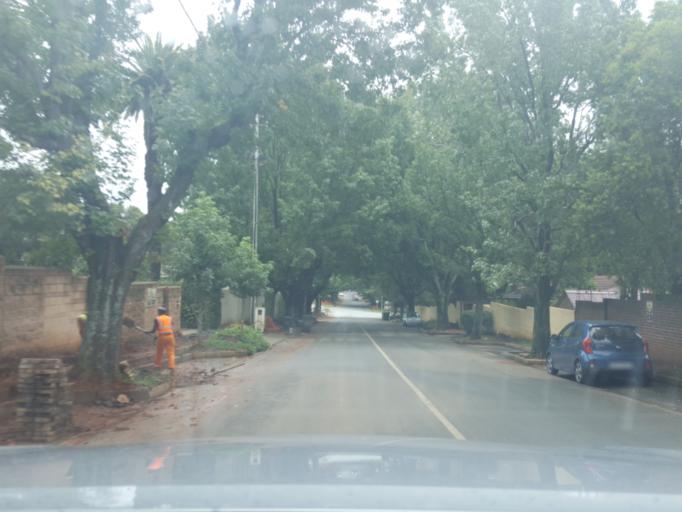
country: ZA
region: Gauteng
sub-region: City of Johannesburg Metropolitan Municipality
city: Johannesburg
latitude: -26.1476
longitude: 28.0135
